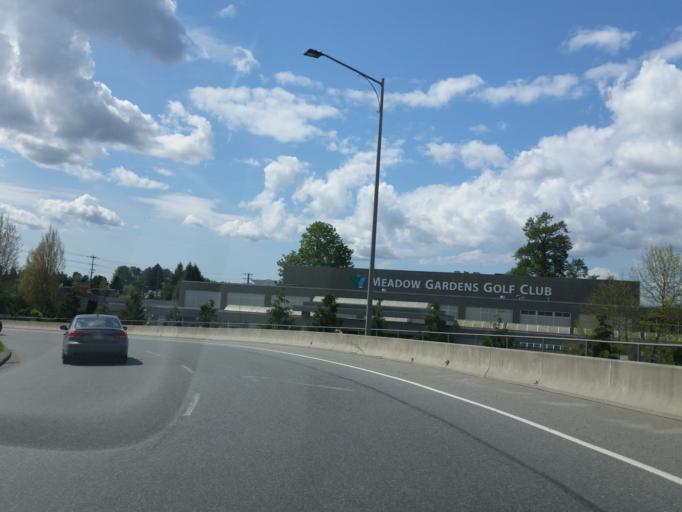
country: CA
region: British Columbia
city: Pitt Meadows
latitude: 49.2246
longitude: -122.6684
